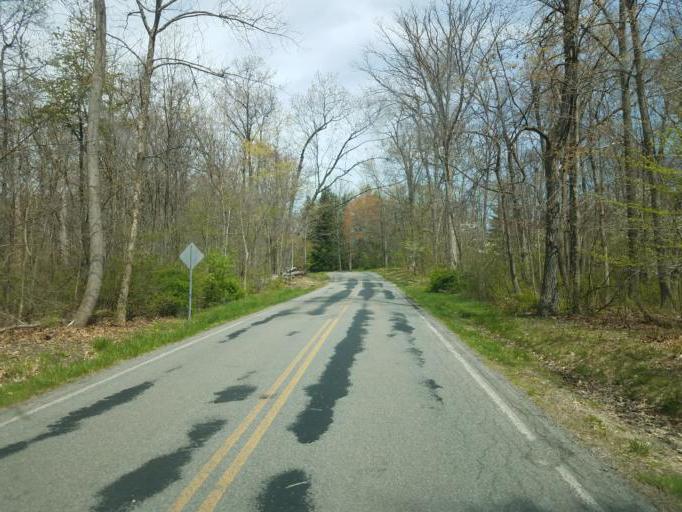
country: US
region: Ohio
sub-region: Summit County
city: Peninsula
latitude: 41.2106
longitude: -81.5802
